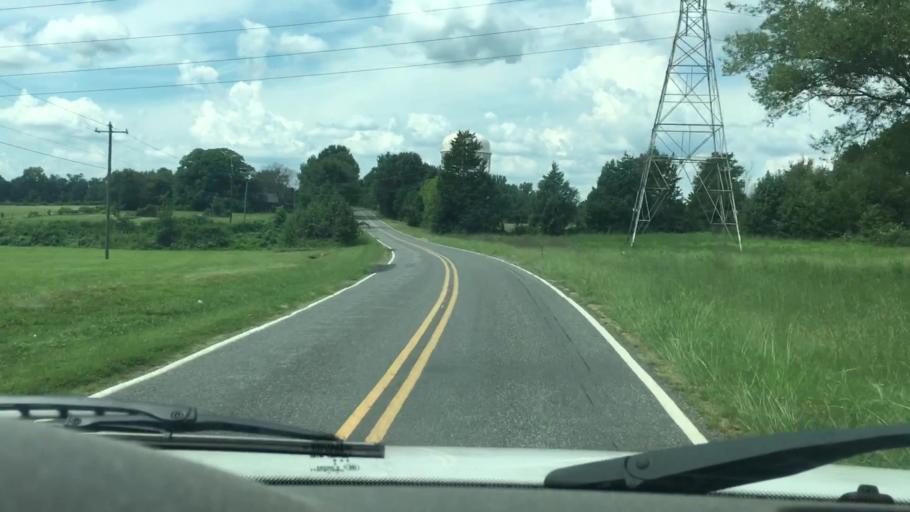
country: US
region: North Carolina
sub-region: Iredell County
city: Troutman
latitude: 35.6786
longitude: -80.8486
